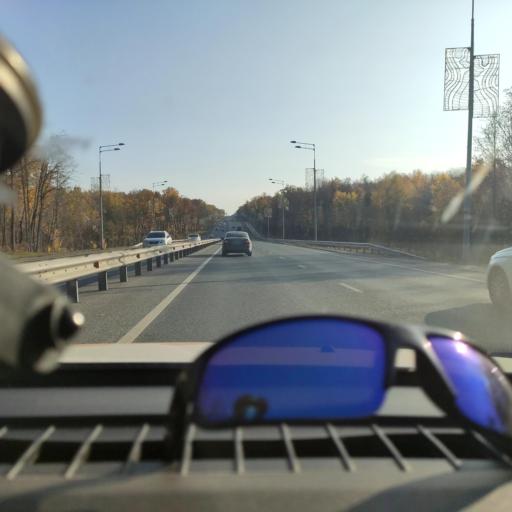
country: RU
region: Samara
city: Novosemeykino
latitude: 53.3354
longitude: 50.2320
